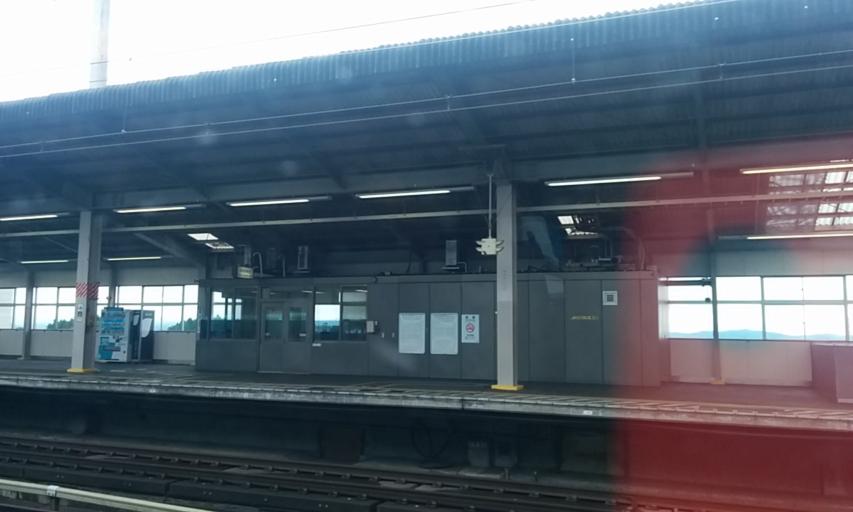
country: JP
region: Tochigi
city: Kuroiso
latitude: 36.9314
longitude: 140.0205
